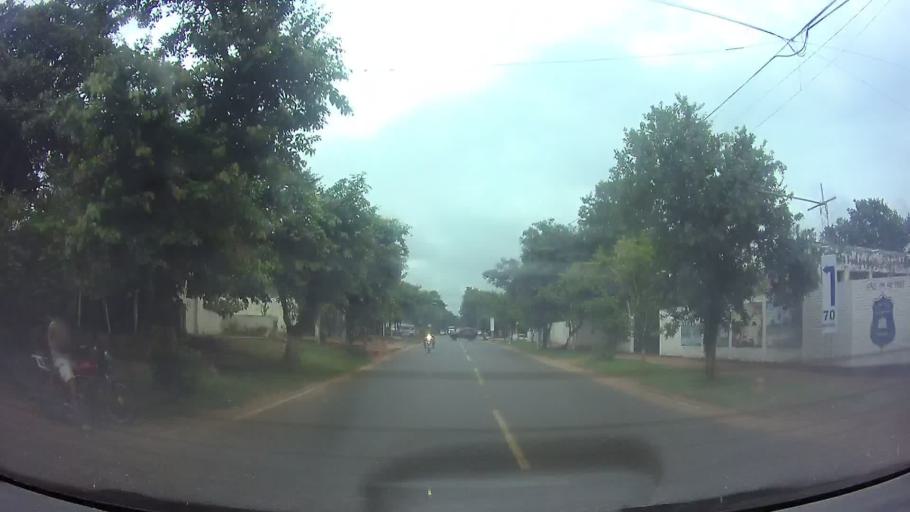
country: PY
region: Paraguari
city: Carapegua
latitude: -25.7675
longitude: -57.2473
